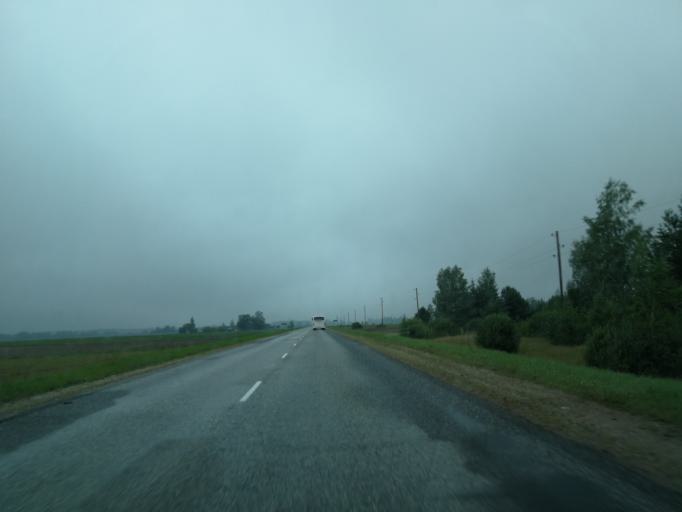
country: LV
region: Preilu Rajons
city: Preili
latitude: 56.3071
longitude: 26.5950
